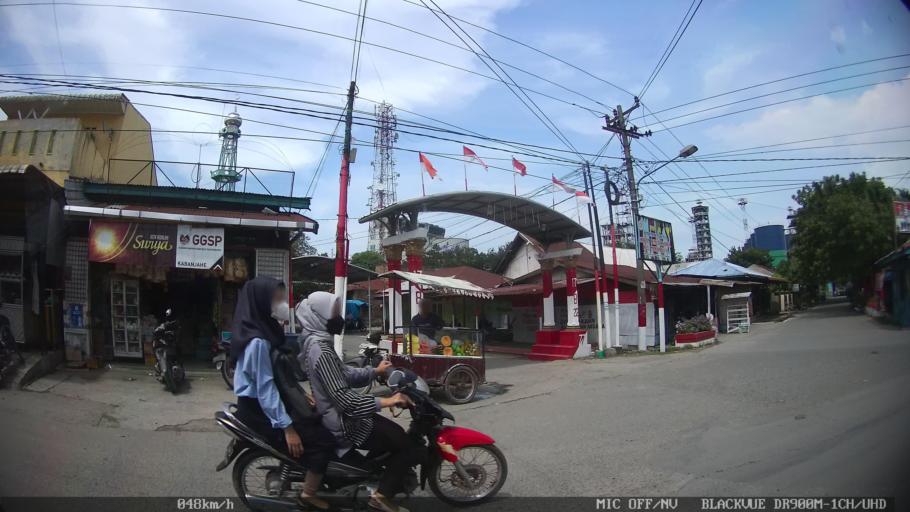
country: ID
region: North Sumatra
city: Labuhan Deli
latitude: 3.6682
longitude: 98.6802
